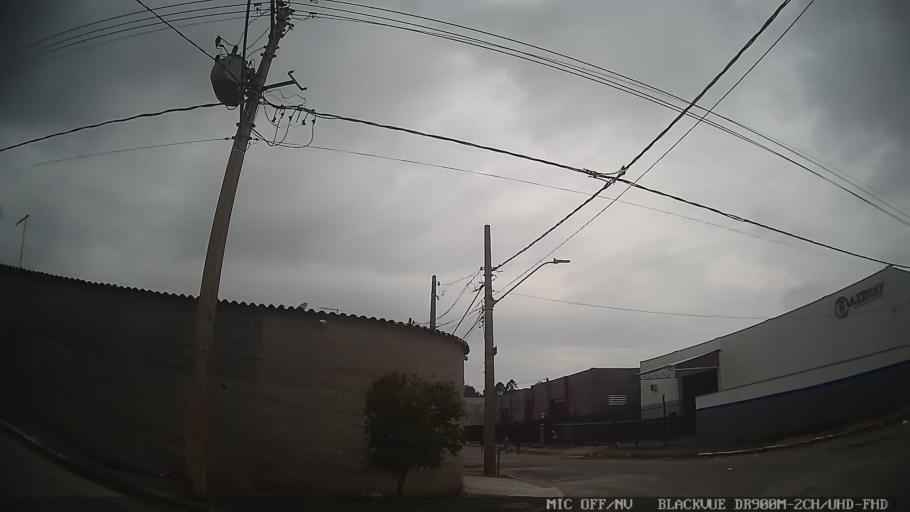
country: BR
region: Sao Paulo
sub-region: Mogi das Cruzes
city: Mogi das Cruzes
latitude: -23.5131
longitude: -46.2087
